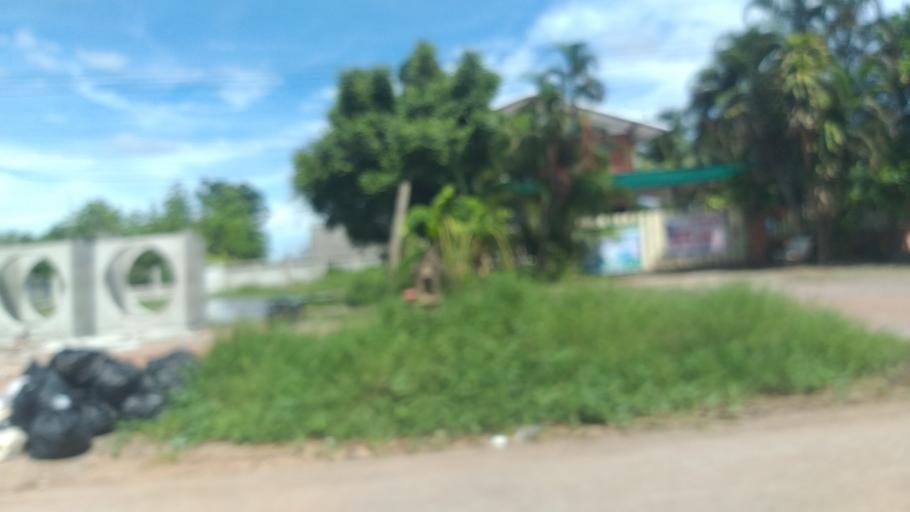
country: TH
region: Khon Kaen
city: Nong Ruea
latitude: 16.4894
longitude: 102.4350
